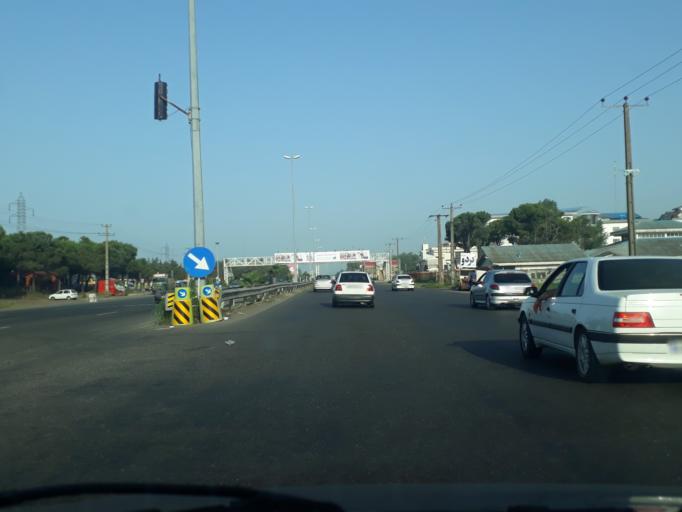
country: IR
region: Gilan
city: Bandar-e Anzali
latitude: 37.4616
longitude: 49.5657
